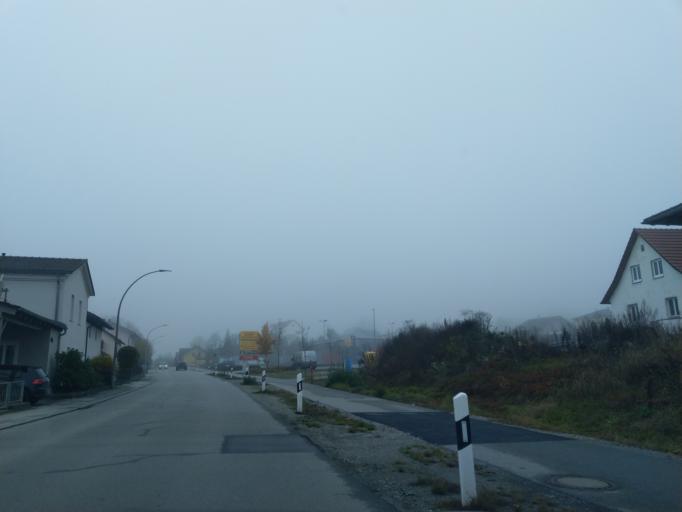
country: DE
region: Bavaria
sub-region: Lower Bavaria
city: Hengersberg
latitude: 48.7730
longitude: 13.0589
